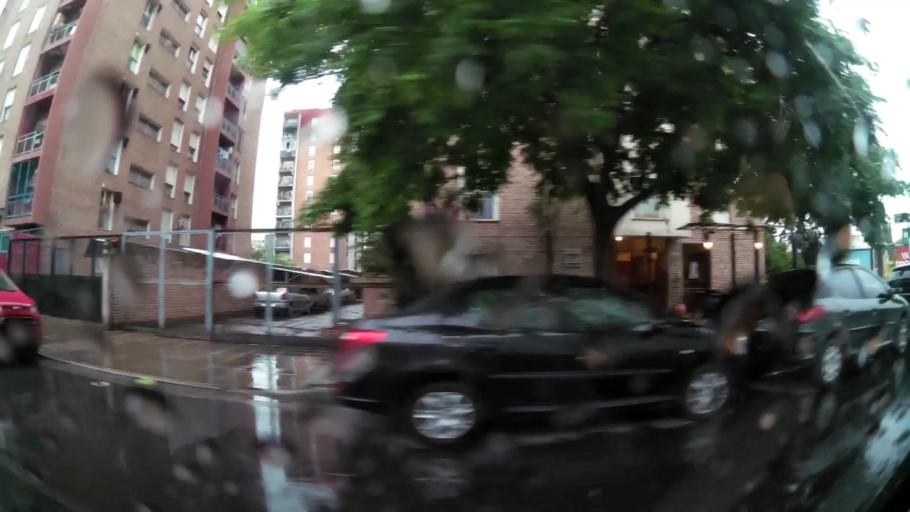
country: AR
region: Buenos Aires F.D.
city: Buenos Aires
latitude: -34.6294
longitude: -58.3674
